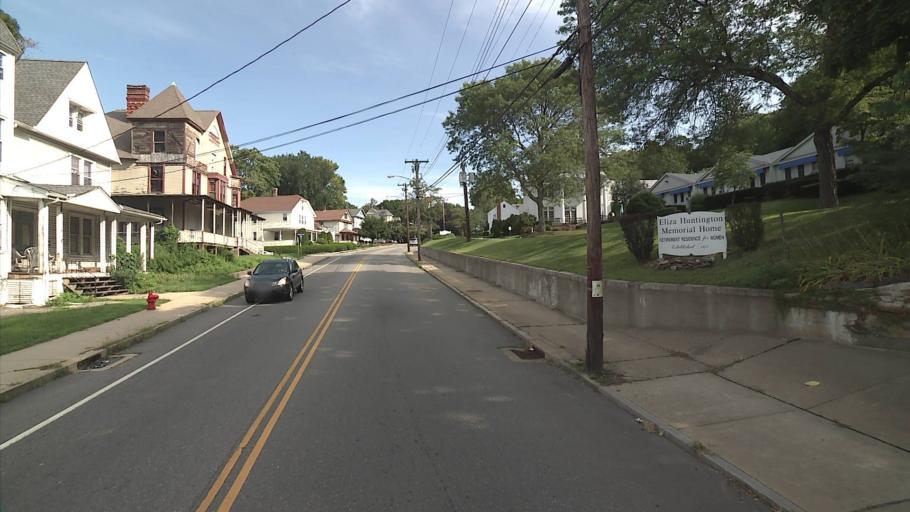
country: US
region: Connecticut
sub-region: New London County
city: Norwich
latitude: 41.5276
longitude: -72.0825
